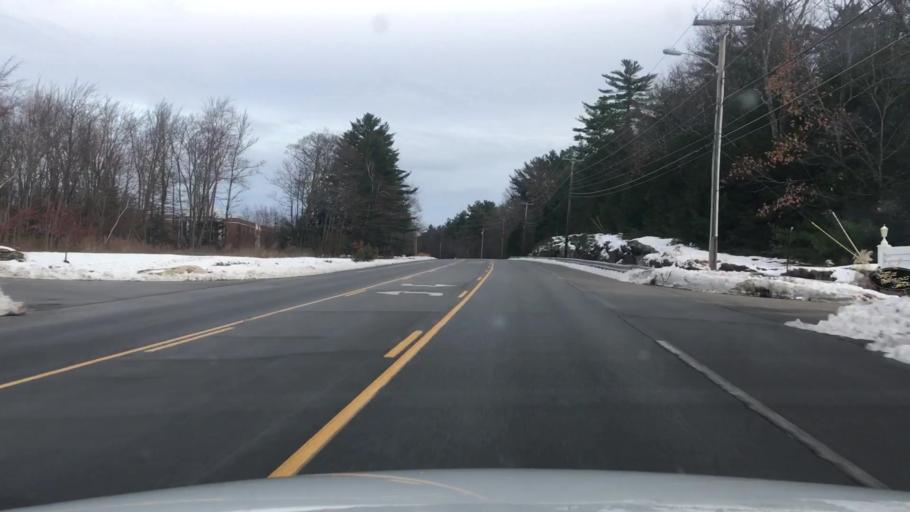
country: US
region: Maine
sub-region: Cumberland County
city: Falmouth Foreside
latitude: 43.7521
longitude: -70.2102
